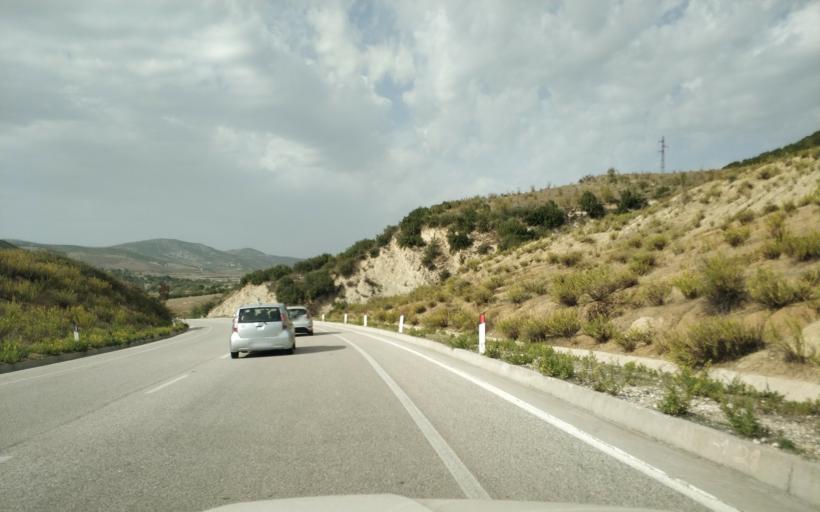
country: AL
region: Gjirokaster
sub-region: Rrethi i Tepelenes
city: Krahes
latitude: 40.4022
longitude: 19.8635
